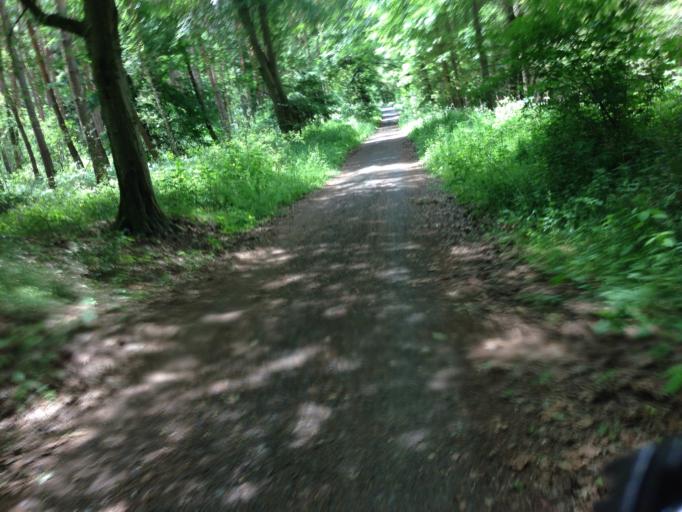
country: DE
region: Hesse
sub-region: Regierungsbezirk Darmstadt
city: Hanau am Main
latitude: 50.1571
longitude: 8.8999
